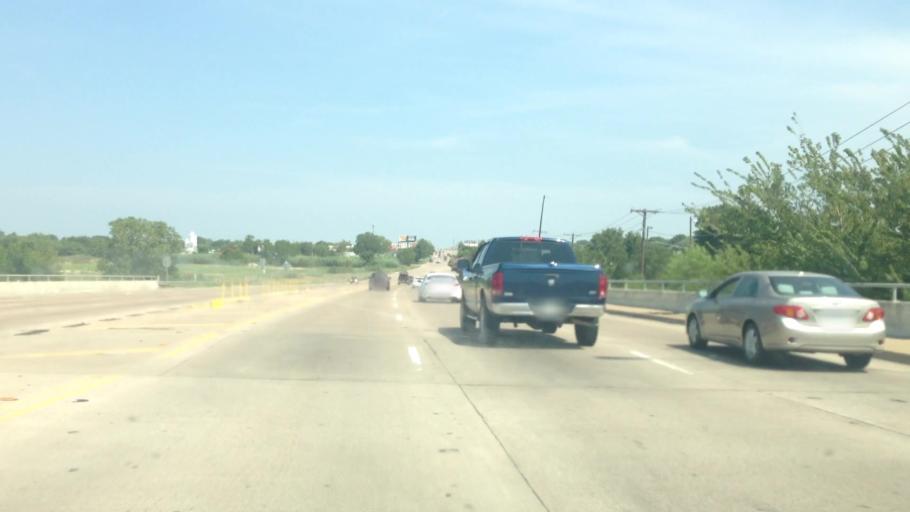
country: US
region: Texas
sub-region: Tarrant County
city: Watauga
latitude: 32.8407
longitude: -97.2641
